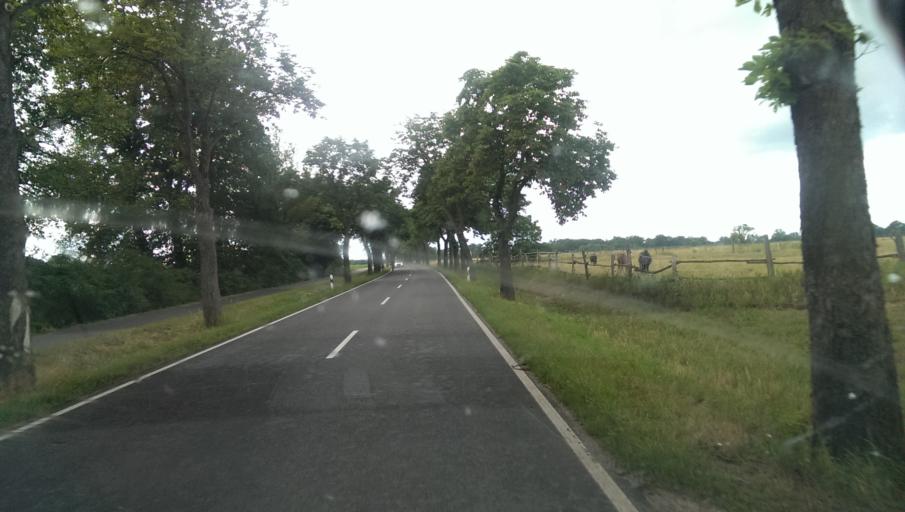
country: DE
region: Brandenburg
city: Stahnsdorf
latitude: 52.3368
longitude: 13.1864
